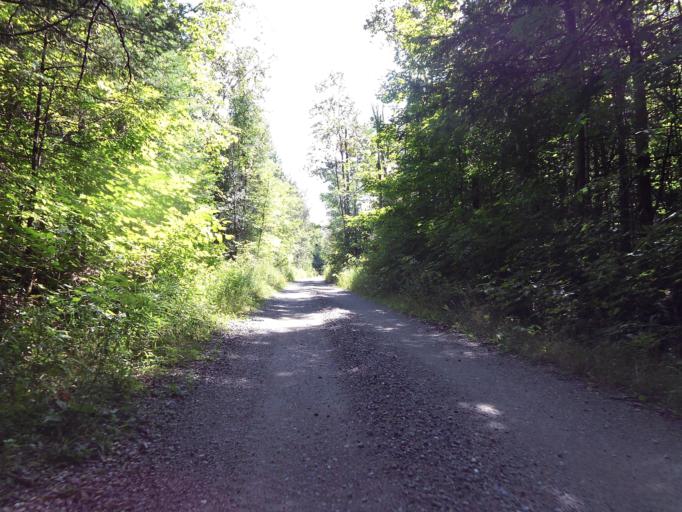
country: CA
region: Ontario
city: Renfrew
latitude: 45.0277
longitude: -76.7049
